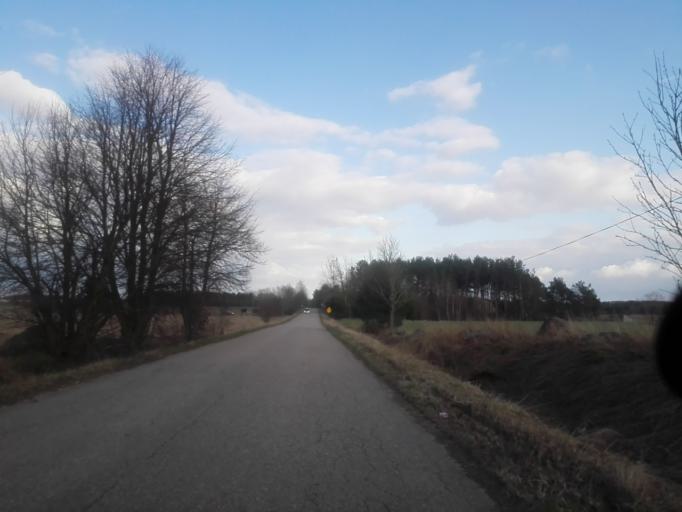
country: PL
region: Podlasie
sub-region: Suwalki
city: Suwalki
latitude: 54.2186
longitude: 22.8499
